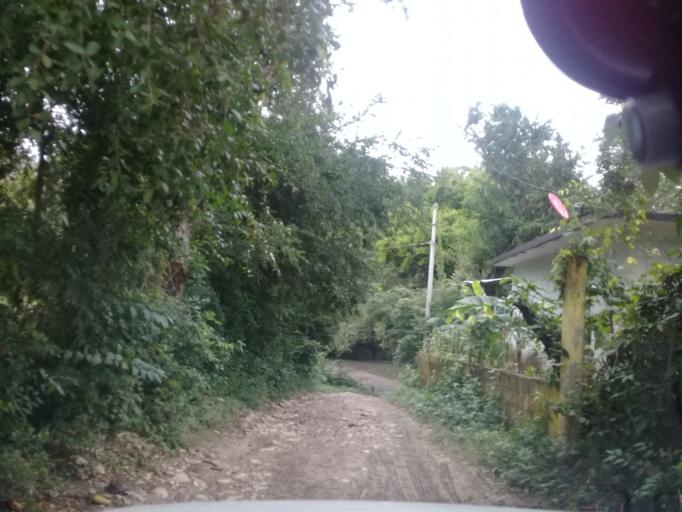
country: MX
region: Veracruz
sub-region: Chalma
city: San Pedro Coyutla
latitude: 21.2046
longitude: -98.3952
